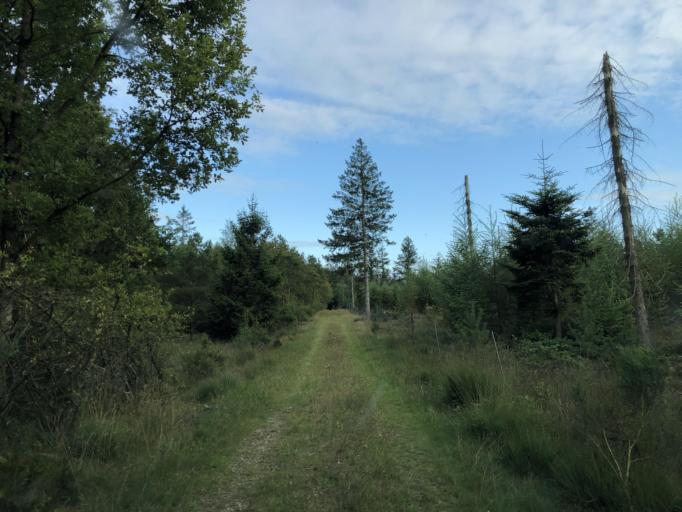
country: DK
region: Central Jutland
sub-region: Holstebro Kommune
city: Ulfborg
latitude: 56.2825
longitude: 8.4216
